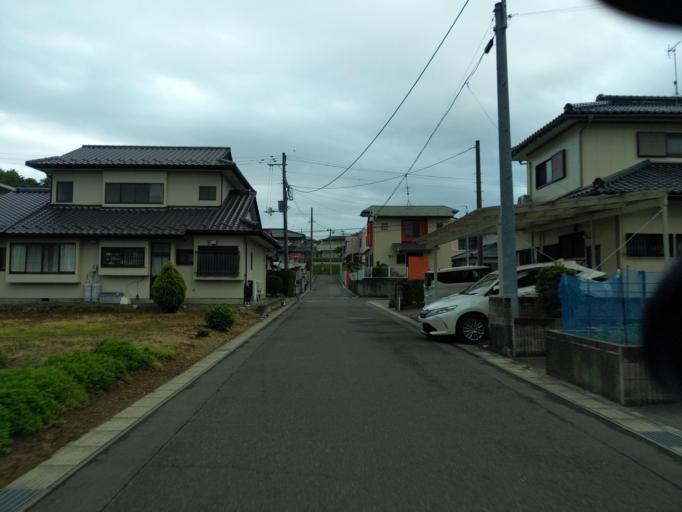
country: JP
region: Fukushima
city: Koriyama
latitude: 37.3659
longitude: 140.3587
